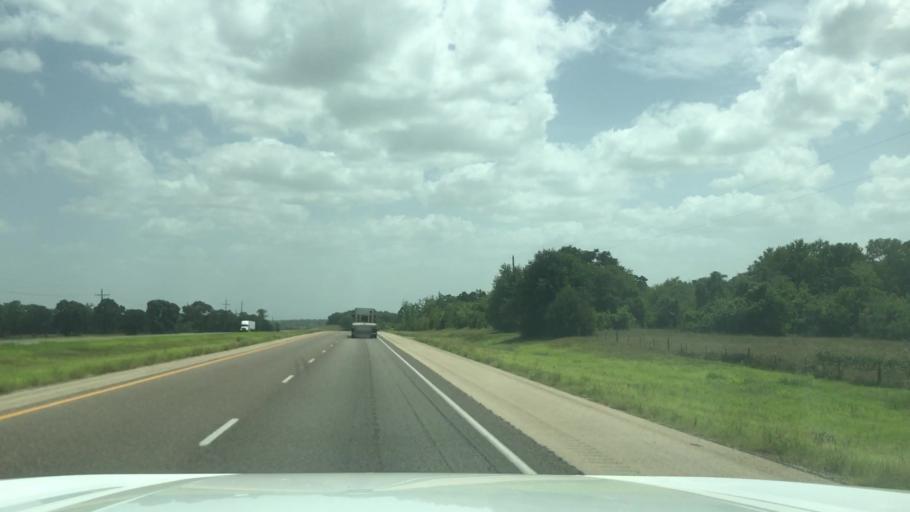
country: US
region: Texas
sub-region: Robertson County
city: Calvert
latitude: 31.0309
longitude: -96.7096
